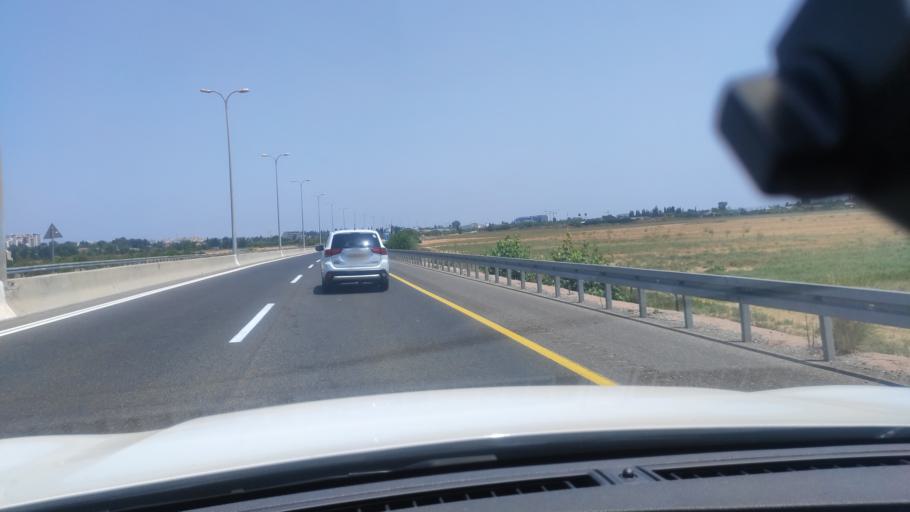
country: IL
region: Central District
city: Hod HaSharon
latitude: 32.1430
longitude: 34.9179
